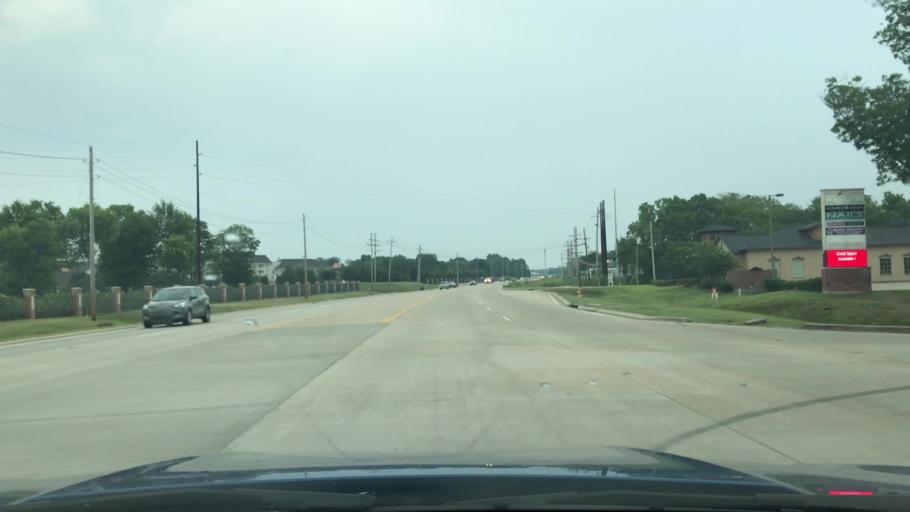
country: US
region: Louisiana
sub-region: Bossier Parish
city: Bossier City
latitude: 32.4008
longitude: -93.7104
